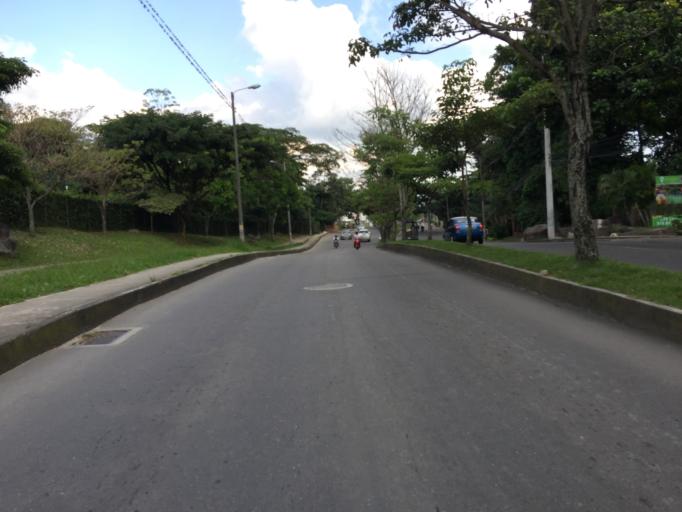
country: CO
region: Tolima
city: Ibague
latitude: 4.4479
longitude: -75.1963
